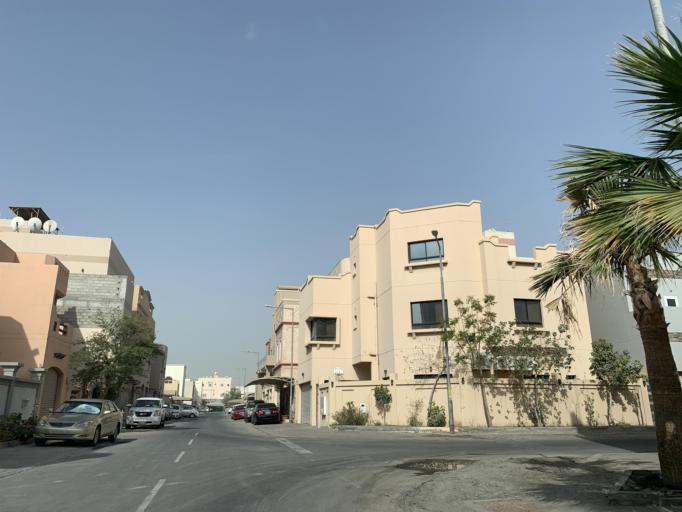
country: BH
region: Northern
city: Madinat `Isa
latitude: 26.1795
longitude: 50.5654
